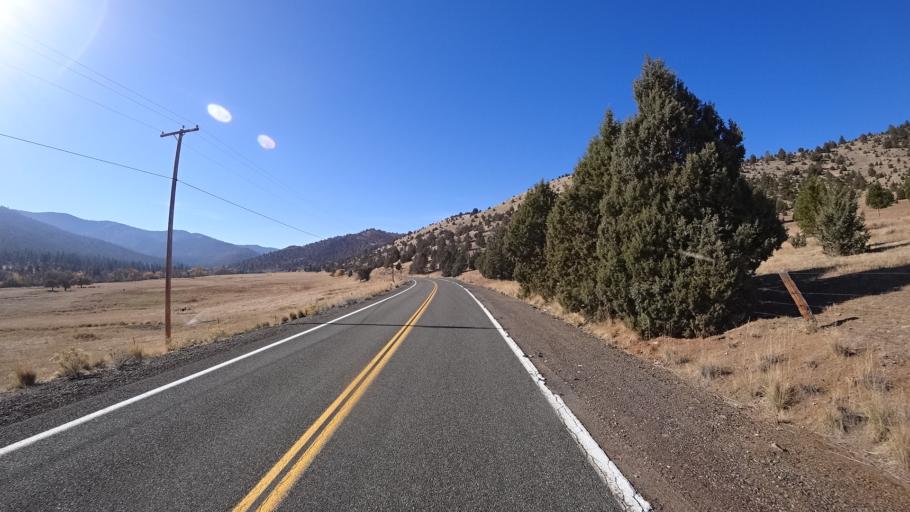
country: US
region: California
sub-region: Siskiyou County
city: Weed
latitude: 41.4894
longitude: -122.5630
